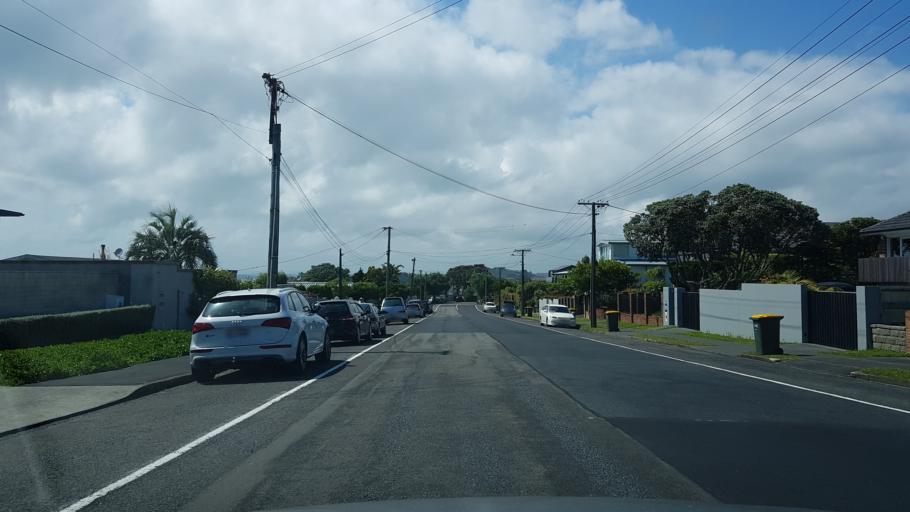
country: NZ
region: Auckland
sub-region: Auckland
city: North Shore
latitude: -36.8081
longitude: 174.7968
